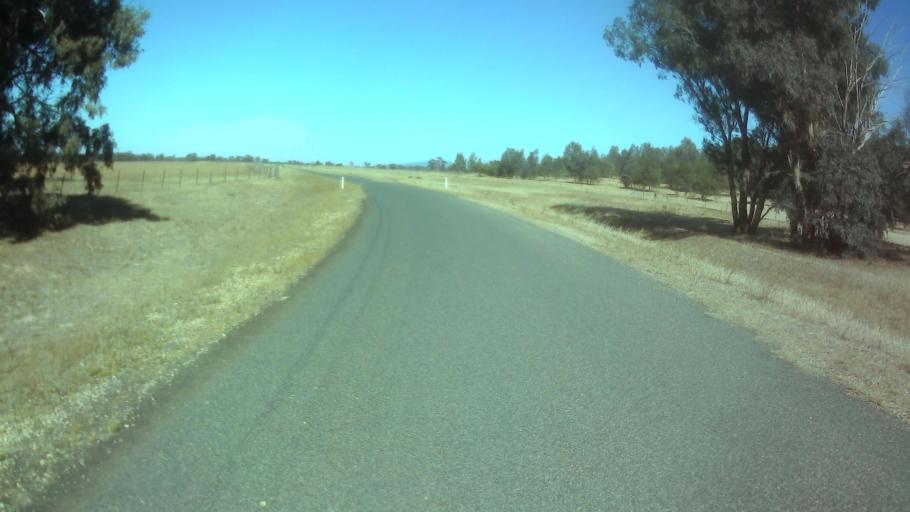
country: AU
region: New South Wales
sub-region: Weddin
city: Grenfell
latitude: -33.9957
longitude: 148.3877
